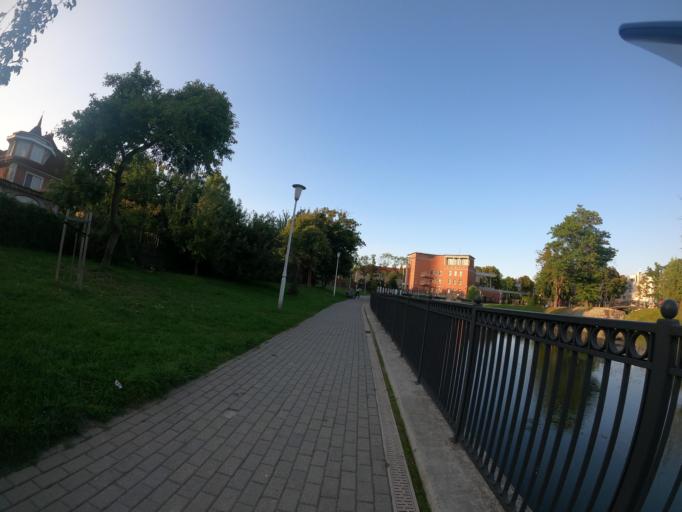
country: RU
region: Kaliningrad
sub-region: Gorod Kaliningrad
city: Kaliningrad
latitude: 54.7215
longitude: 20.4609
